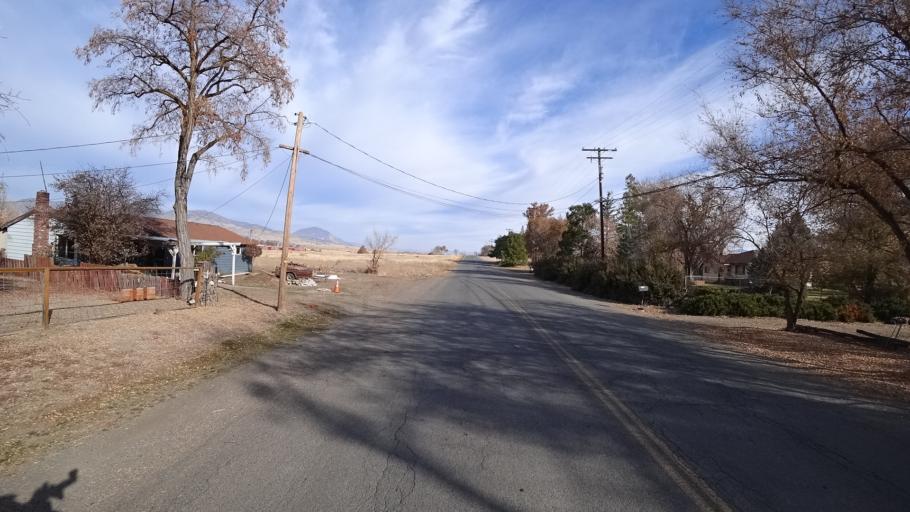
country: US
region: California
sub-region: Siskiyou County
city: Montague
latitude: 41.7298
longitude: -122.5227
